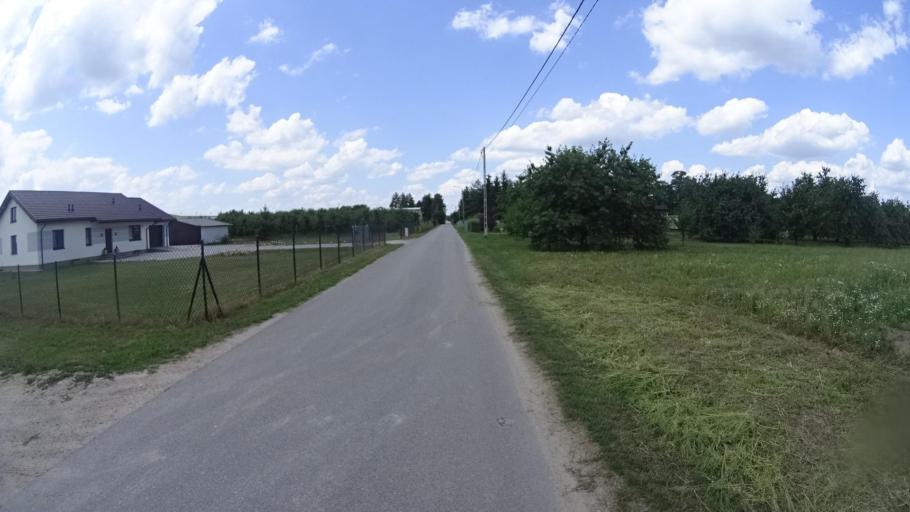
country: PL
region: Masovian Voivodeship
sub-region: Powiat bialobrzeski
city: Promna
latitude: 51.7074
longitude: 20.9196
